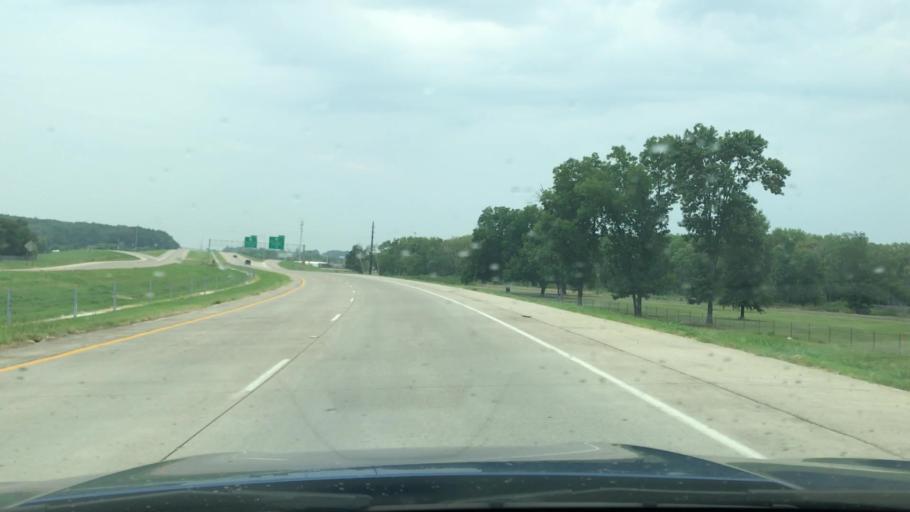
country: US
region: Louisiana
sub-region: Bossier Parish
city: Bossier City
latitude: 32.4091
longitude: -93.7171
